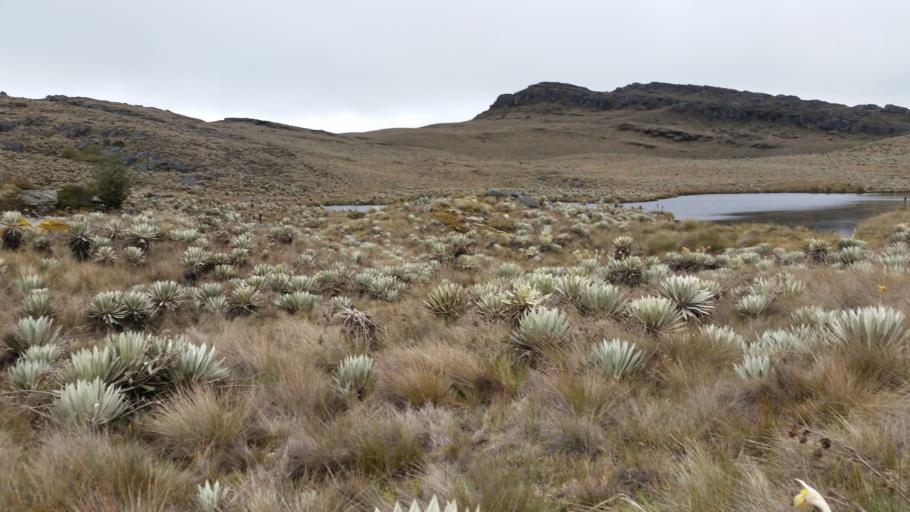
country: CO
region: Cundinamarca
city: Pasca
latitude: 4.3686
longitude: -74.2143
